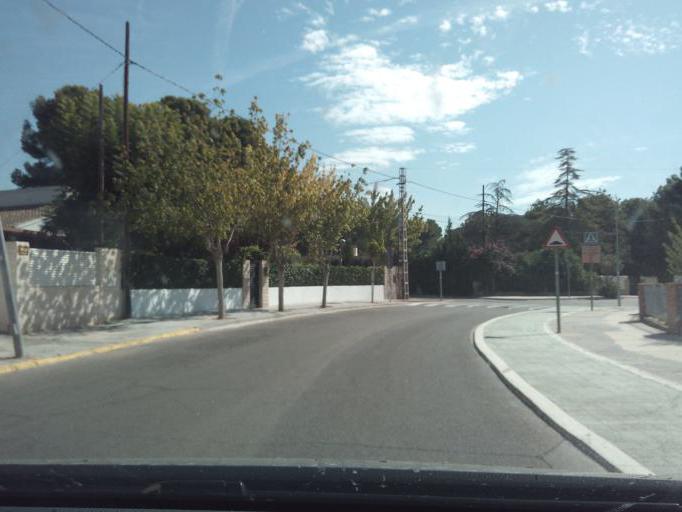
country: ES
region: Valencia
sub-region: Provincia de Valencia
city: Betera
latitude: 39.5414
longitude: -0.4829
